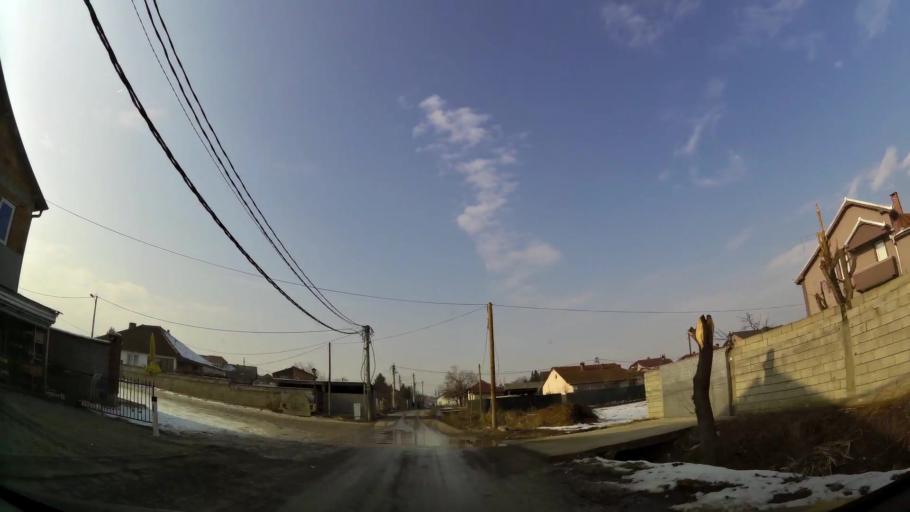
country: MK
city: Creshevo
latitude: 42.0196
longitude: 21.5041
